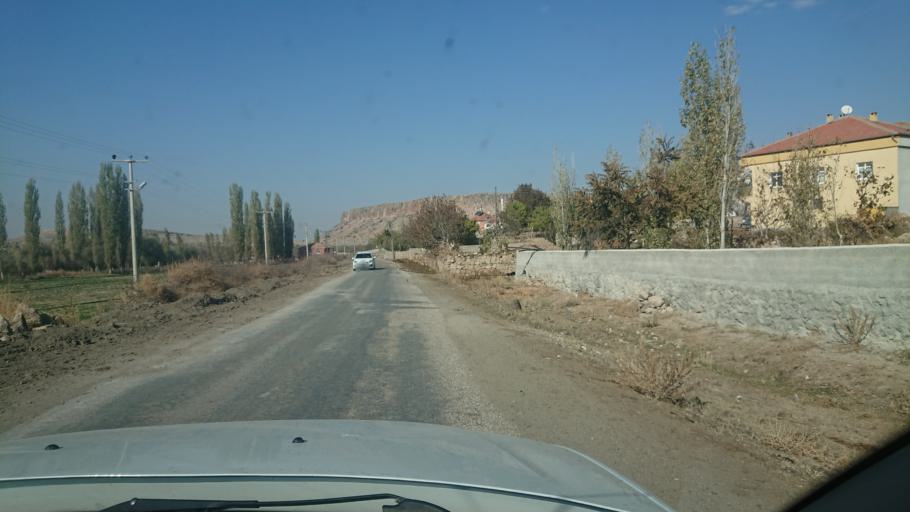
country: TR
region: Aksaray
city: Gulagac
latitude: 38.3524
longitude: 34.2337
